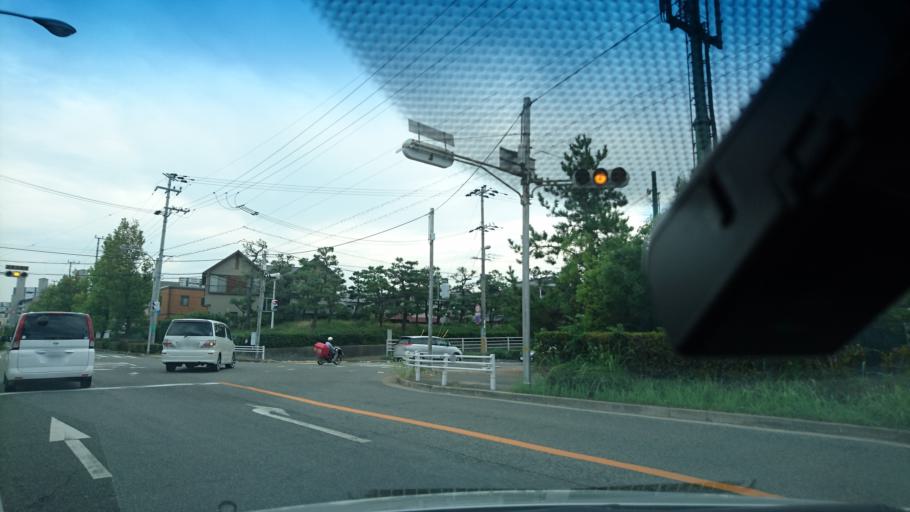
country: JP
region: Hyogo
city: Ashiya
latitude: 34.7194
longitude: 135.3053
